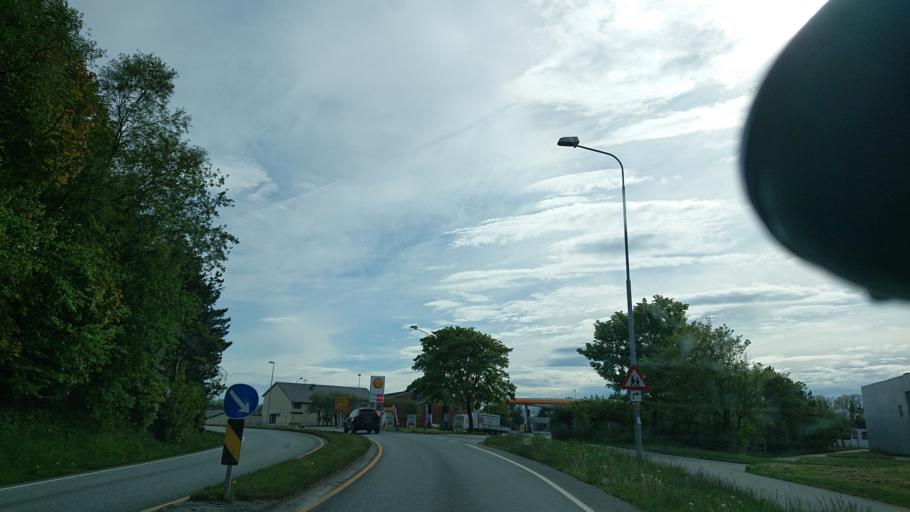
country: NO
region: Rogaland
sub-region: Sola
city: Tananger
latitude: 58.9369
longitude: 5.6052
